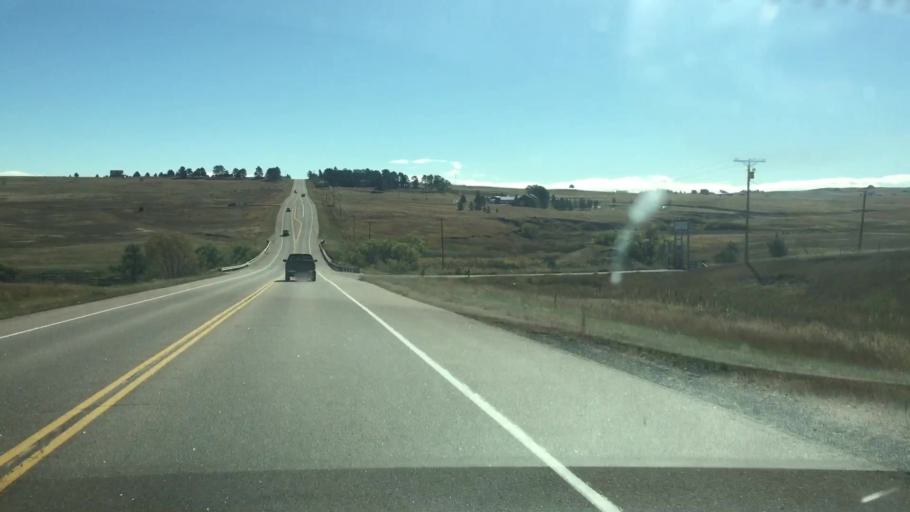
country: US
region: Colorado
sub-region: Elbert County
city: Elizabeth
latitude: 39.3593
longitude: -104.5366
